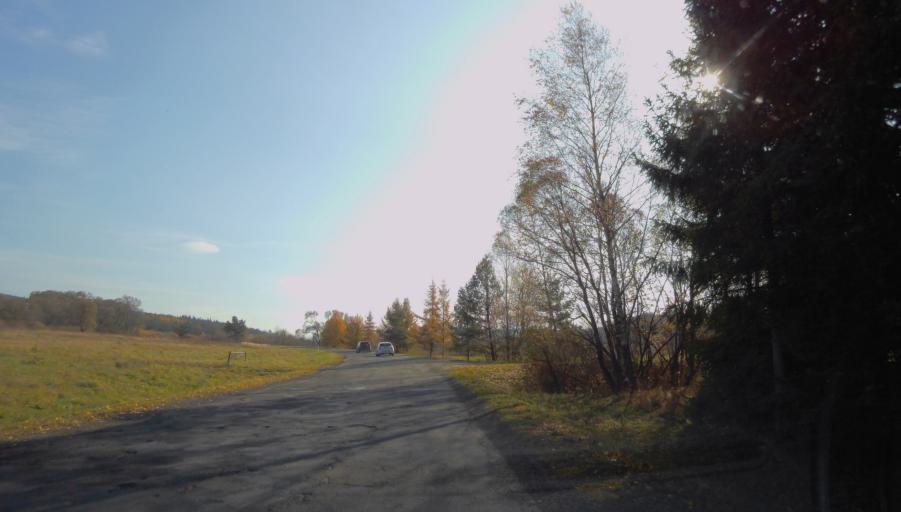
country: PL
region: Subcarpathian Voivodeship
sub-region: Powiat sanocki
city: Komancza
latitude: 49.2427
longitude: 22.1340
